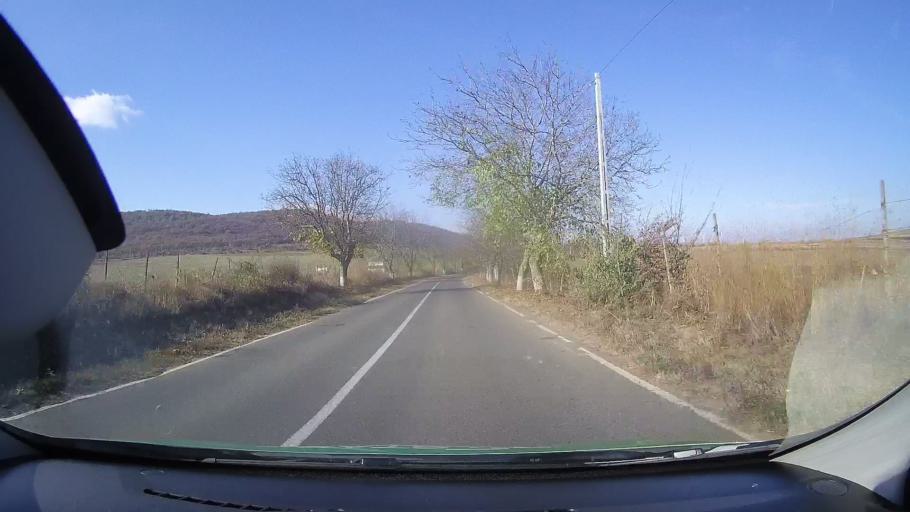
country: RO
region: Tulcea
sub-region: Oras Babadag
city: Babadag
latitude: 44.8803
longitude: 28.7478
